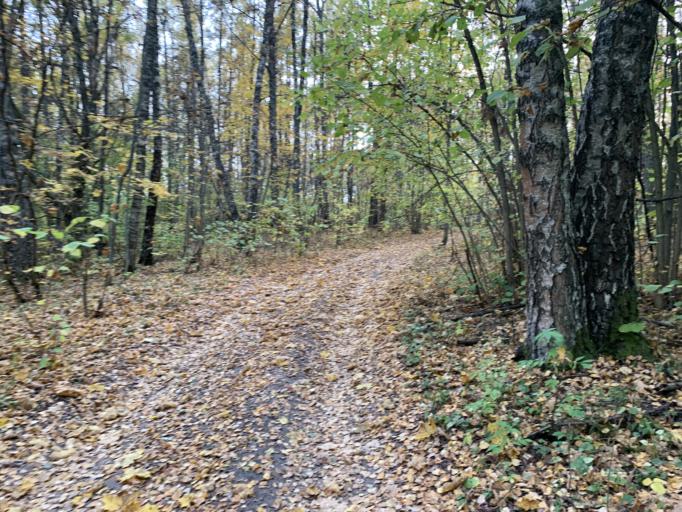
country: RU
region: Jaroslavl
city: Petrovsk
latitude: 56.9837
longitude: 39.3774
